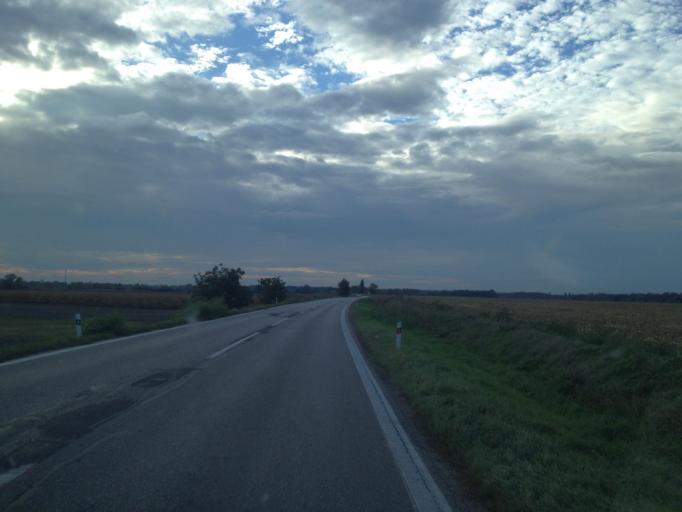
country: SK
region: Nitriansky
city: Komarno
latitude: 47.7615
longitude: 18.1859
